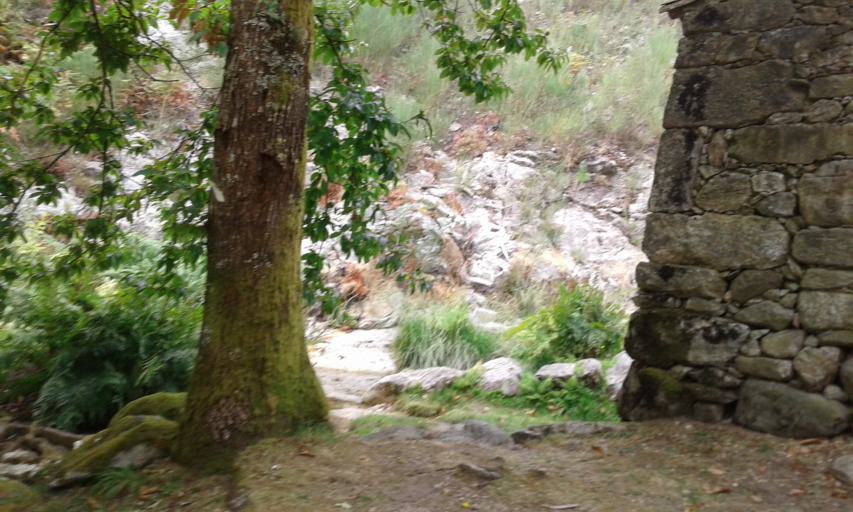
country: ES
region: Galicia
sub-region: Provincia de Pontevedra
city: O Rosal
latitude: 41.9600
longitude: -8.8403
